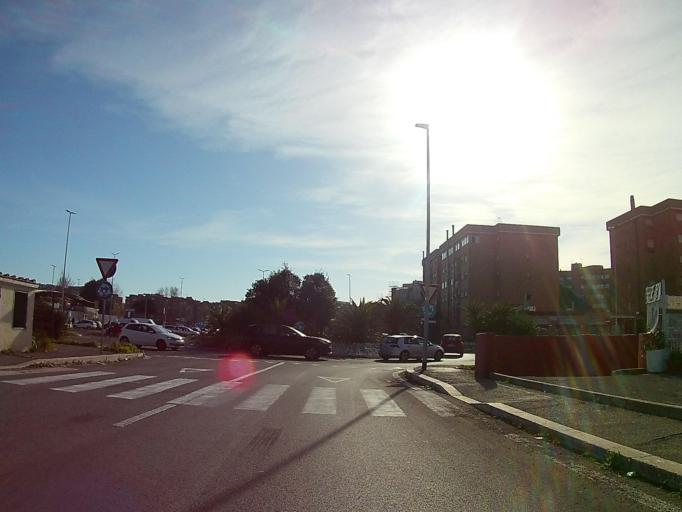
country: IT
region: Latium
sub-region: Citta metropolitana di Roma Capitale
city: Lido di Ostia
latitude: 41.7394
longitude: 12.2617
